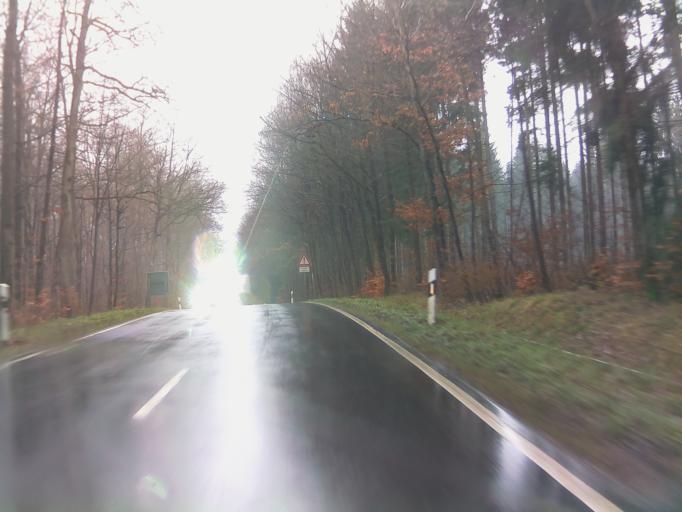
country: DE
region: Hesse
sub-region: Regierungsbezirk Kassel
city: Dipperz
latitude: 50.5584
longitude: 9.8046
